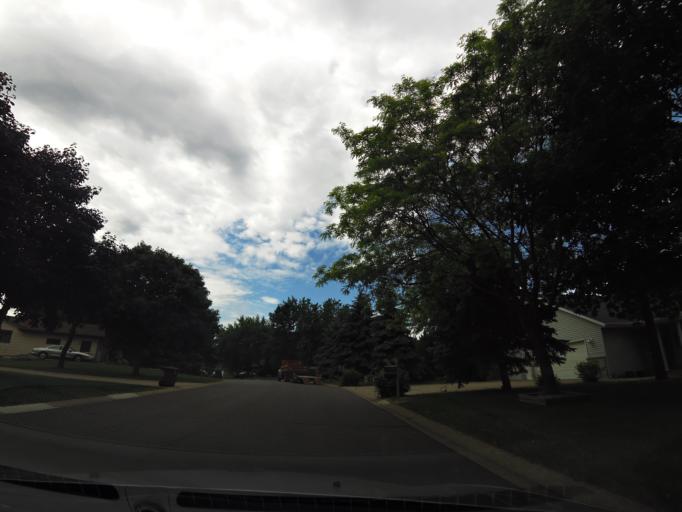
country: US
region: Minnesota
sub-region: Scott County
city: Prior Lake
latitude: 44.7046
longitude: -93.4453
